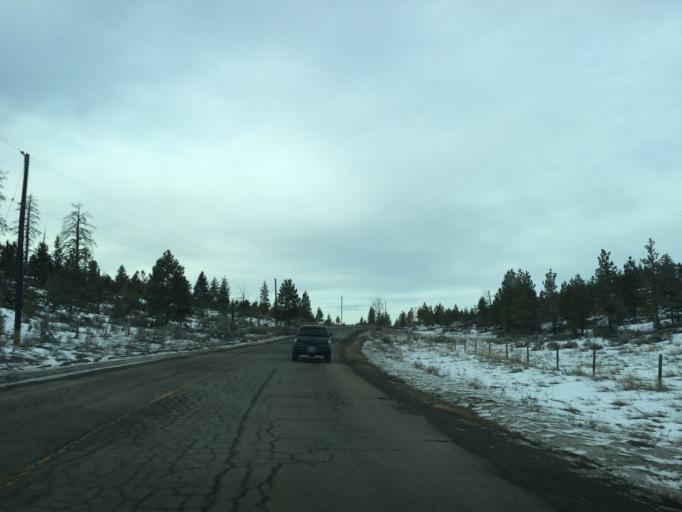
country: CA
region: British Columbia
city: Kamloops
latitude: 50.6377
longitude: -120.4488
